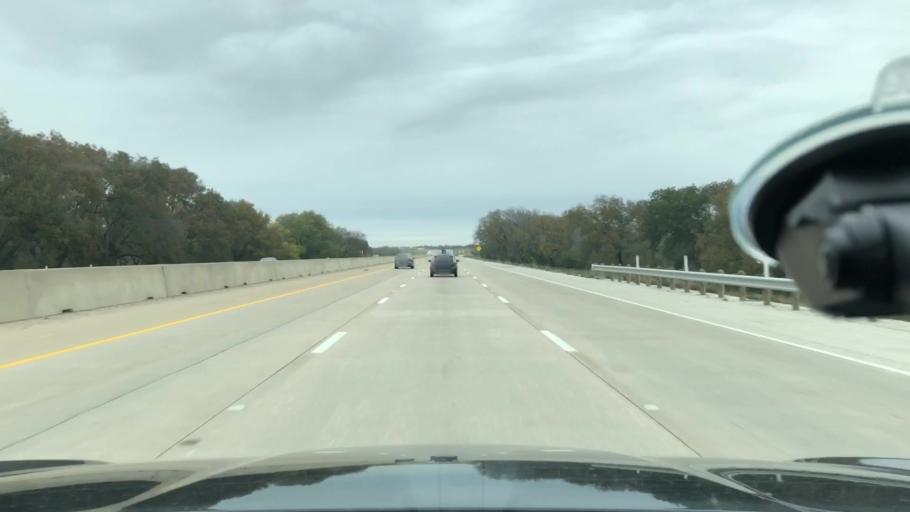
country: US
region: Texas
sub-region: Ellis County
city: Italy
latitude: 32.2282
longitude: -96.8839
